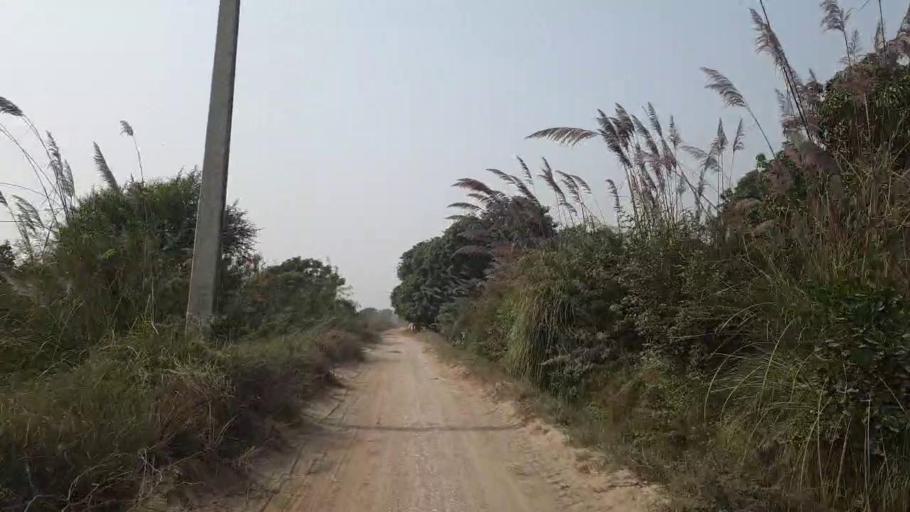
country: PK
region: Sindh
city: Tando Muhammad Khan
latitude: 25.1903
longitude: 68.5902
